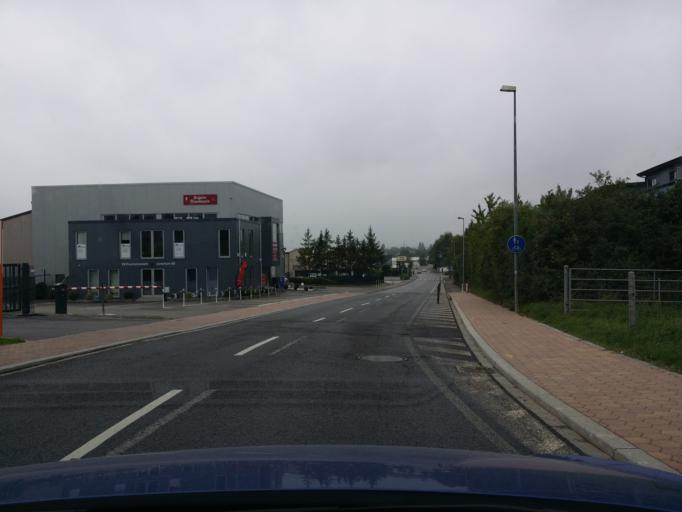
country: LU
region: Luxembourg
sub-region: Canton de Luxembourg
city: Strassen
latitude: 49.6123
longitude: 6.0790
